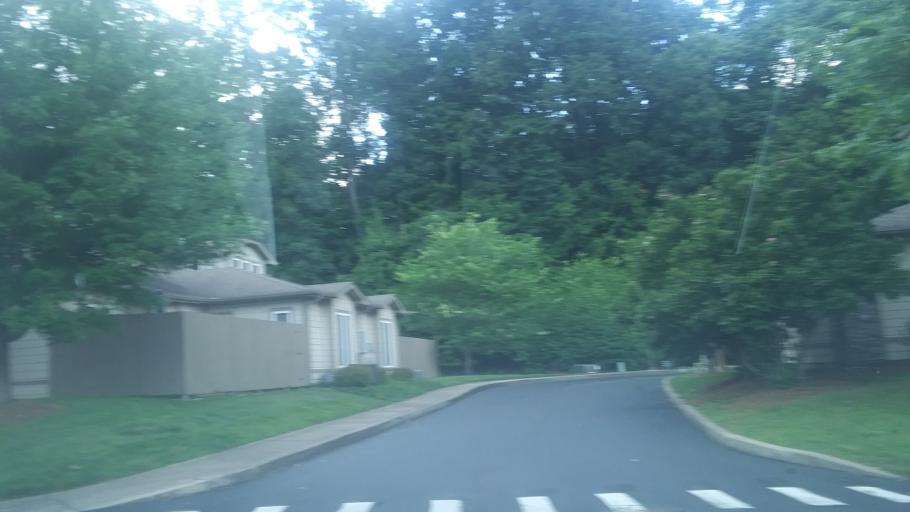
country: US
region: Tennessee
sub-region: Davidson County
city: Belle Meade
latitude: 36.0876
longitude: -86.9173
